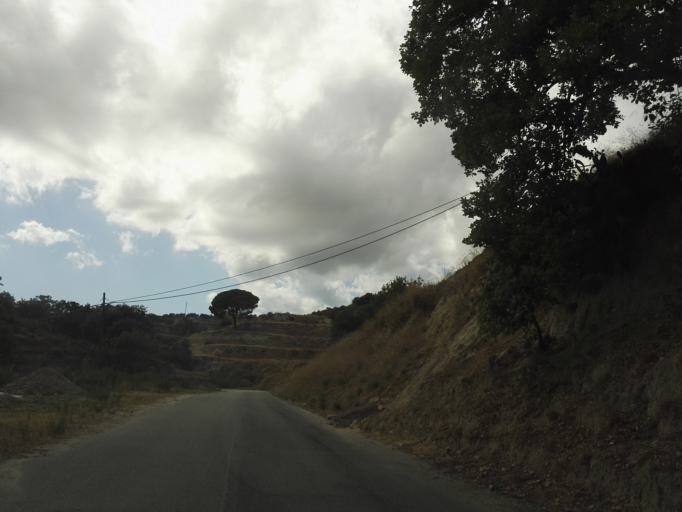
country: IT
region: Calabria
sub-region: Provincia di Reggio Calabria
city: Camini
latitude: 38.4248
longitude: 16.4850
